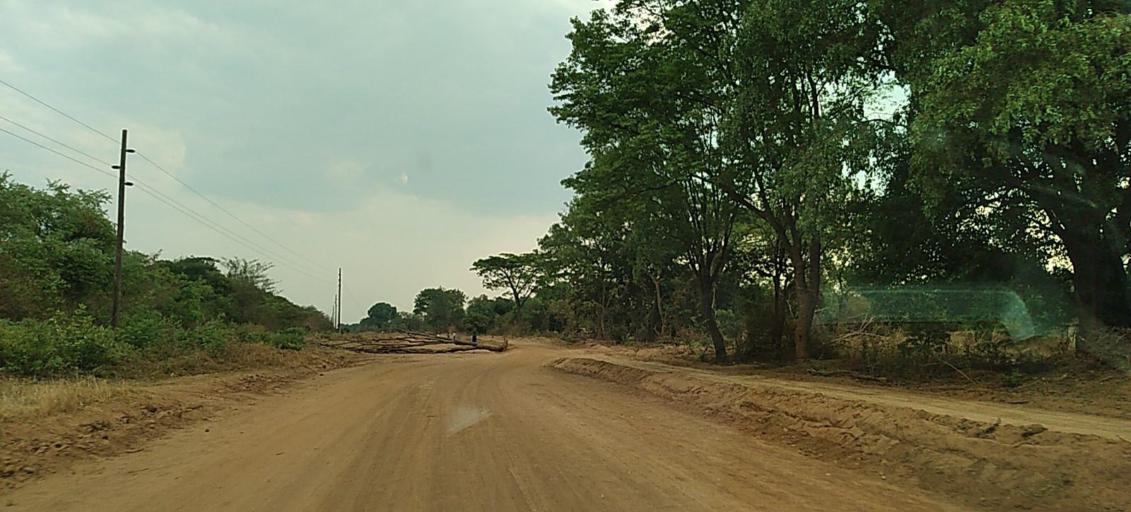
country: ZM
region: Copperbelt
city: Kalulushi
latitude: -12.9012
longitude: 27.9484
